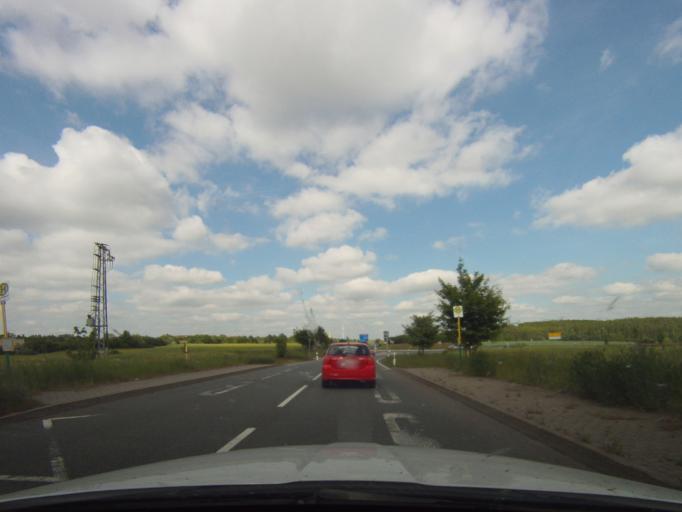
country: DE
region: Thuringia
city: Paitzdorf
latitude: 50.8689
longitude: 12.2193
